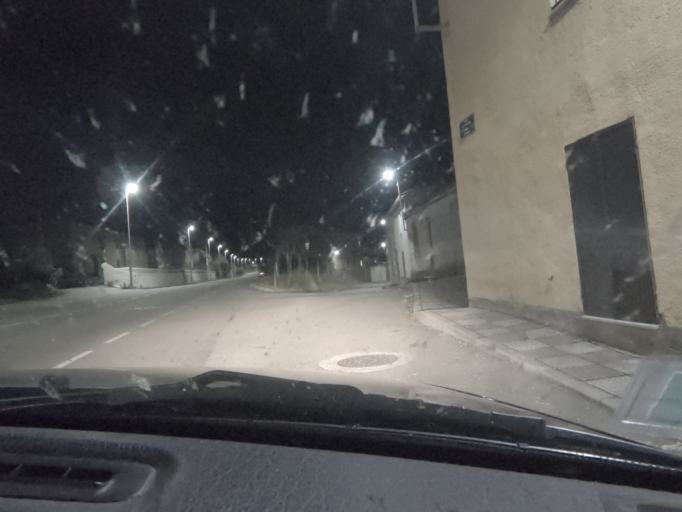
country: ES
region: Castille and Leon
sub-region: Provincia de Salamanca
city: Robleda
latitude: 40.3832
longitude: -6.6105
